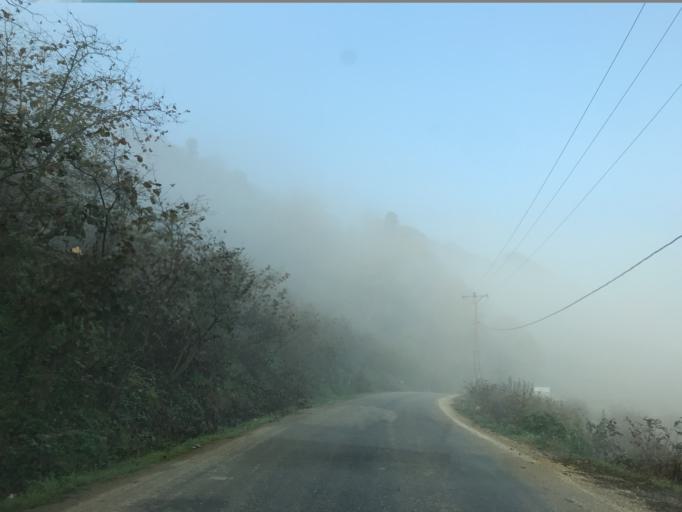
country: TR
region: Duzce
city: Cumayeri
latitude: 40.9079
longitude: 30.9479
